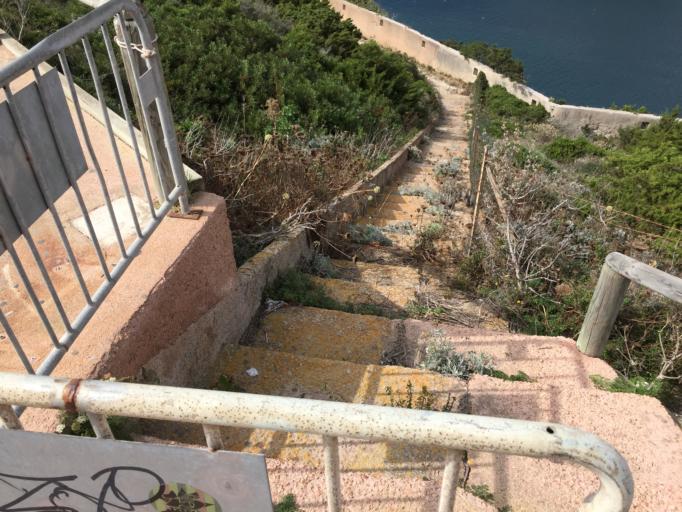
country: FR
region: Corsica
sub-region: Departement de la Corse-du-Sud
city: Bonifacio
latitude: 41.3880
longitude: 9.1526
